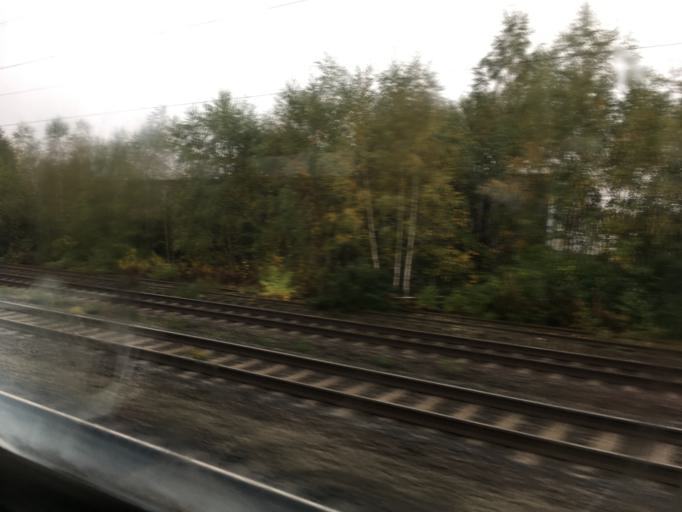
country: DE
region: North Rhine-Westphalia
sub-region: Regierungsbezirk Arnsberg
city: Herne
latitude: 51.5656
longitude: 7.1960
